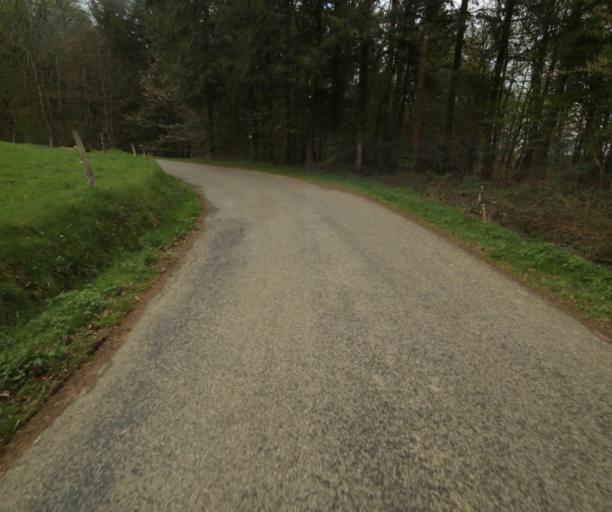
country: FR
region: Limousin
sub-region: Departement de la Correze
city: Laguenne
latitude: 45.2470
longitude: 1.8558
